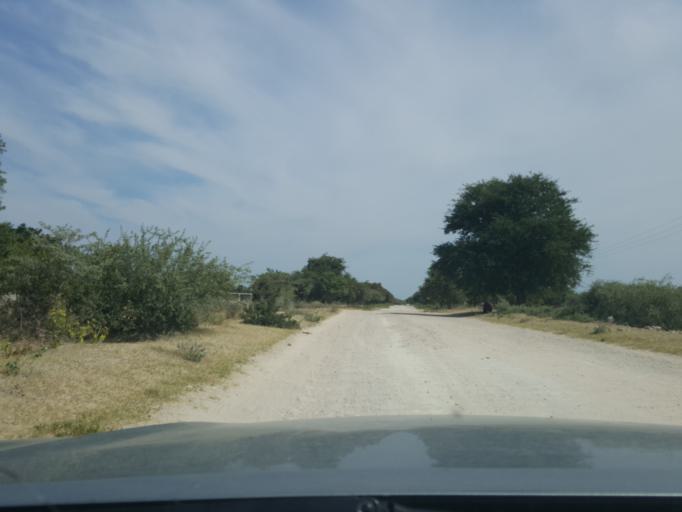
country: BW
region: North West
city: Shakawe
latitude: -18.3157
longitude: 21.9024
